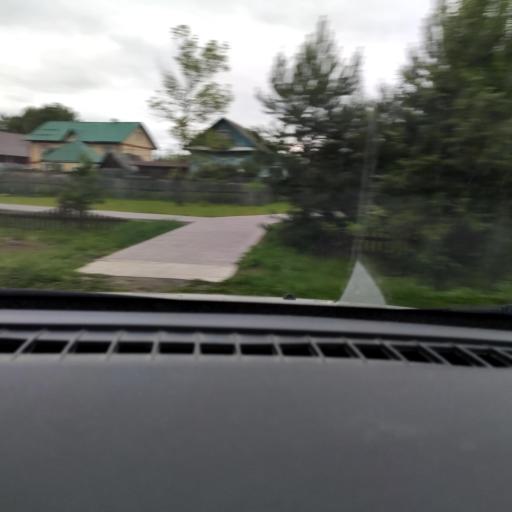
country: RU
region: Perm
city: Perm
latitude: 58.0321
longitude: 56.2313
